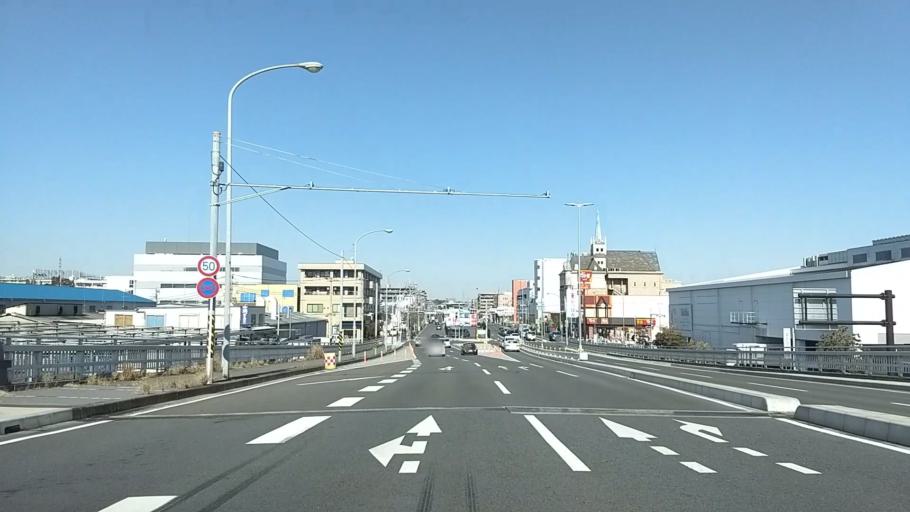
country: JP
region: Kanagawa
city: Yokohama
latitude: 35.5152
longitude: 139.6130
